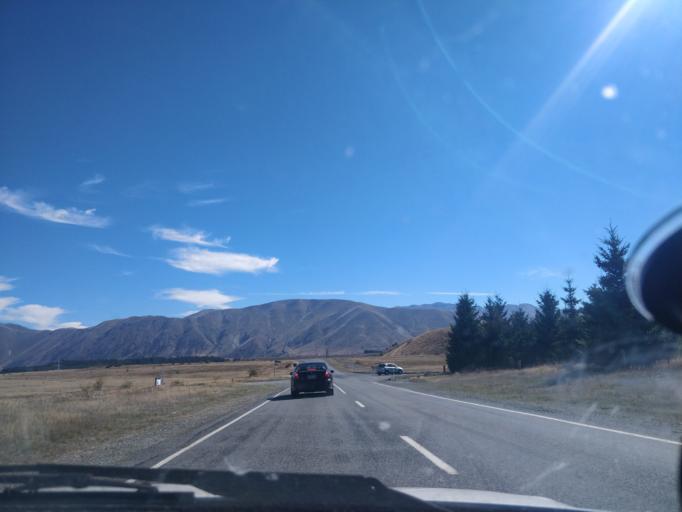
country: NZ
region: Otago
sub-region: Queenstown-Lakes District
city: Wanaka
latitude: -44.2681
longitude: 170.0401
